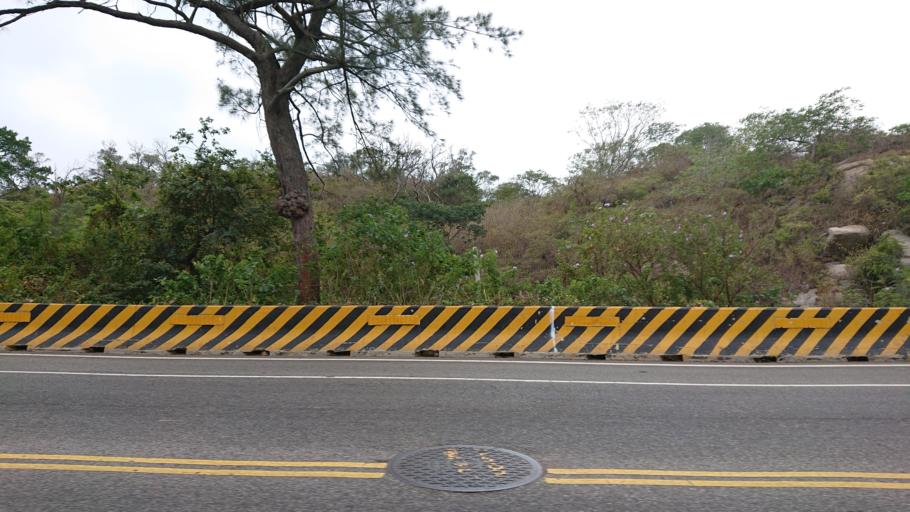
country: TW
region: Fukien
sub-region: Kinmen
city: Jincheng
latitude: 24.4399
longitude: 118.3927
